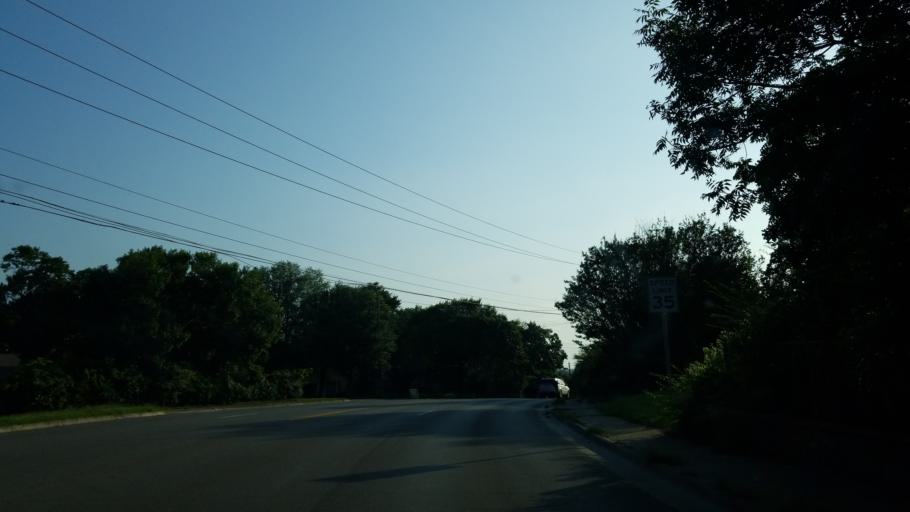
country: US
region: Texas
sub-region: Denton County
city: Denton
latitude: 33.2324
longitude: -97.1304
